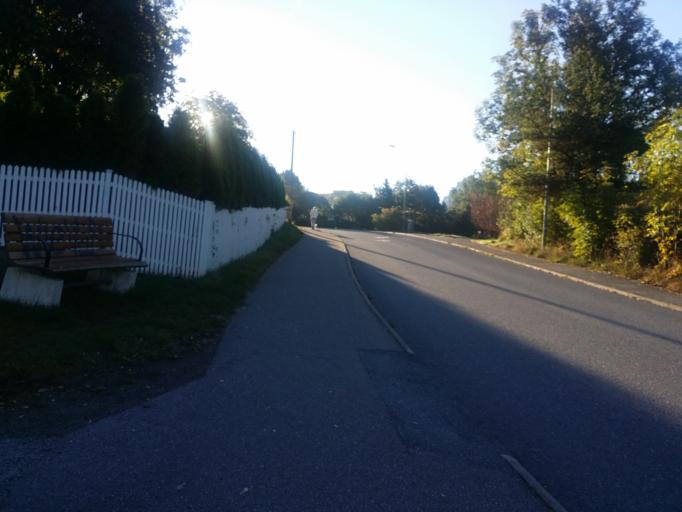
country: SE
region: Stockholm
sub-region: Upplands-Bro Kommun
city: Kungsaengen
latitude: 59.4810
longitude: 17.7443
